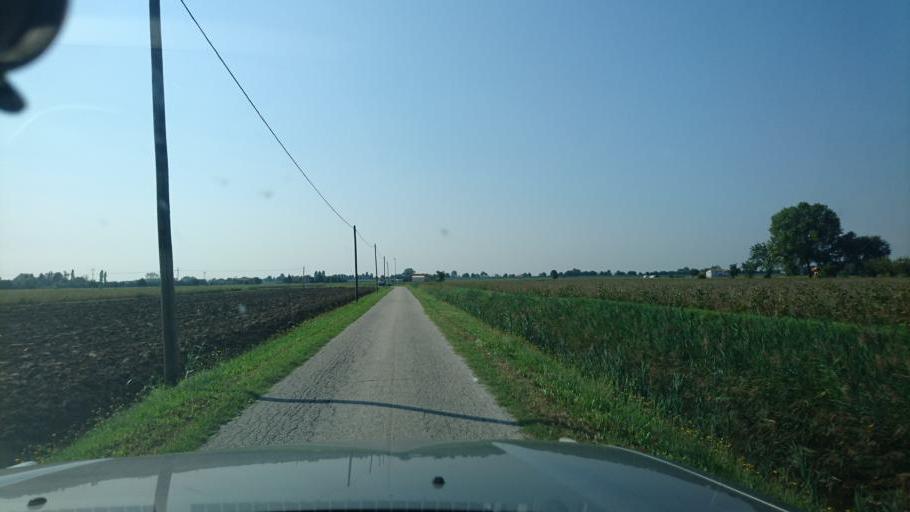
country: IT
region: Veneto
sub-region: Provincia di Padova
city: Bovolenta
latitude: 45.2863
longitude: 11.9173
